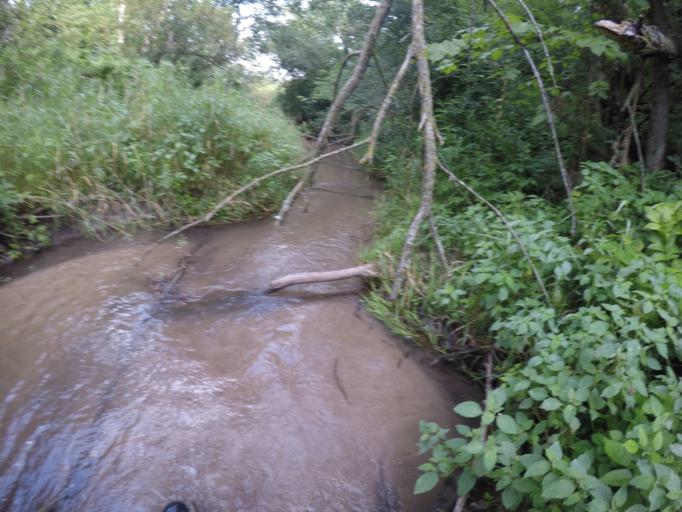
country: US
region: Minnesota
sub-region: Olmsted County
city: Eyota
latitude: 43.9801
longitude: -92.3351
